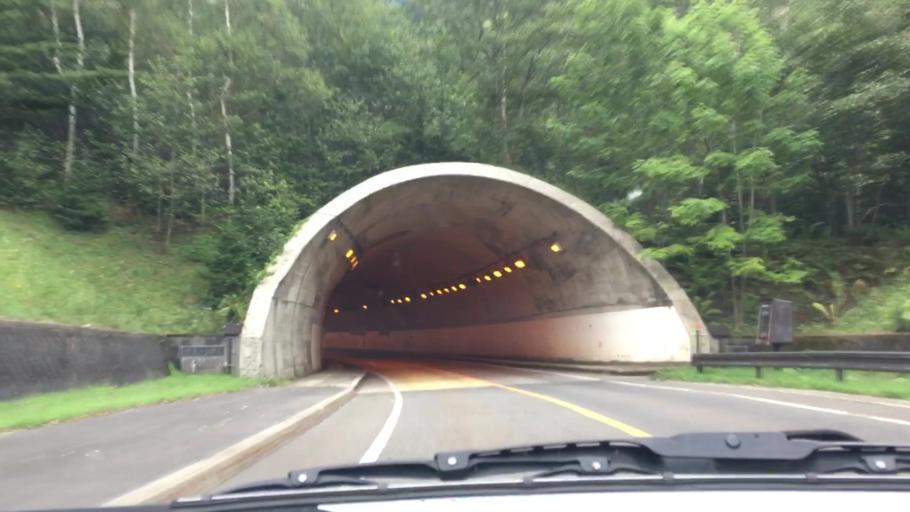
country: JP
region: Hokkaido
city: Otofuke
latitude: 43.3629
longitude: 143.2359
